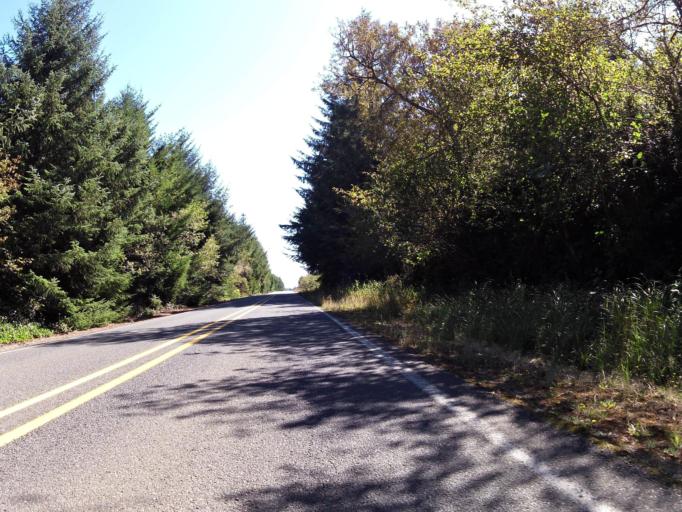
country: US
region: Oregon
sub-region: Coos County
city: Barview
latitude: 43.2629
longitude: -124.3429
